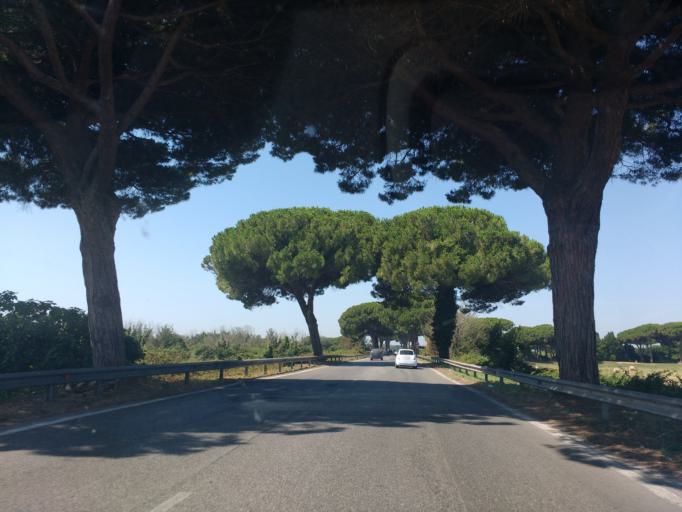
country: IT
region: Latium
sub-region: Citta metropolitana di Roma Capitale
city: Lido di Ostia
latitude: 41.7536
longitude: 12.2948
